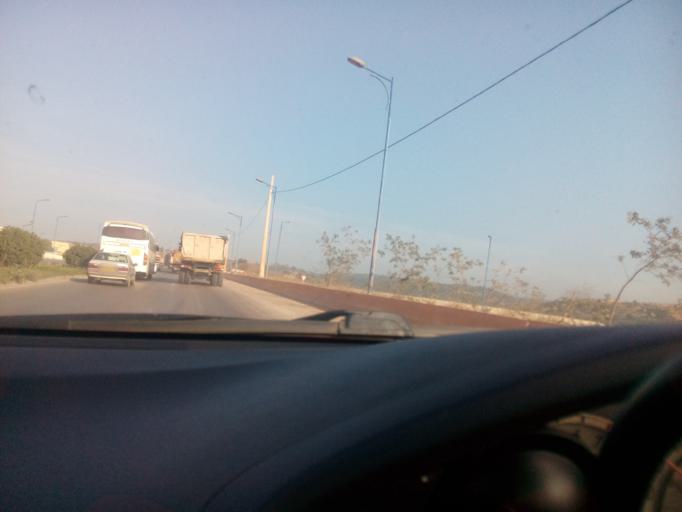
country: DZ
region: Oran
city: Es Senia
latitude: 35.6255
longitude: -0.7187
